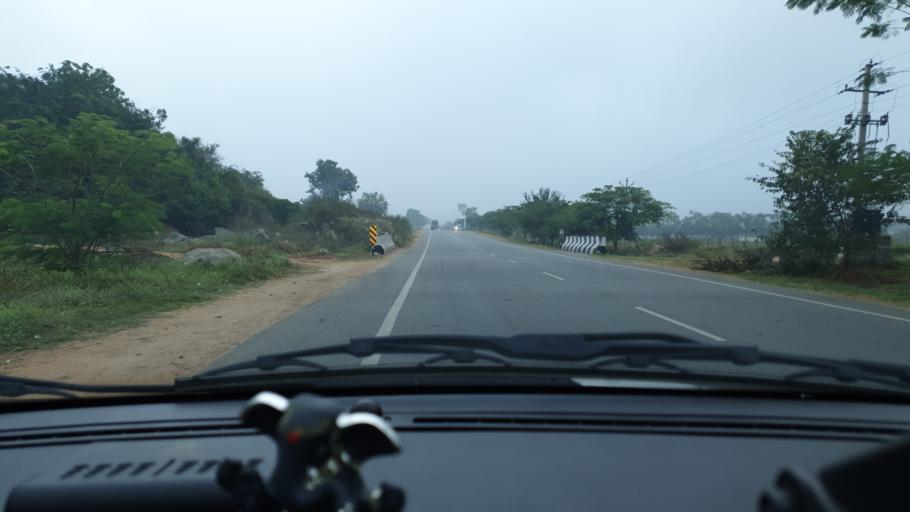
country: IN
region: Telangana
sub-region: Mahbubnagar
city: Farrukhnagar
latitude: 16.9643
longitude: 78.5105
